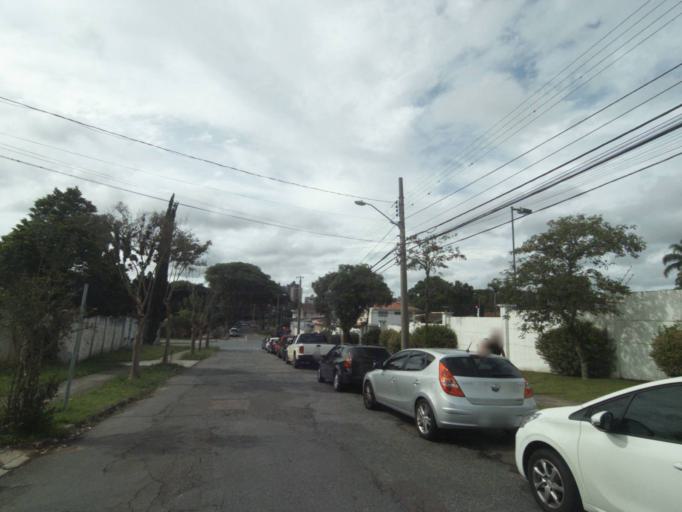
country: BR
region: Parana
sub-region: Curitiba
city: Curitiba
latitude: -25.4415
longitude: -49.2999
